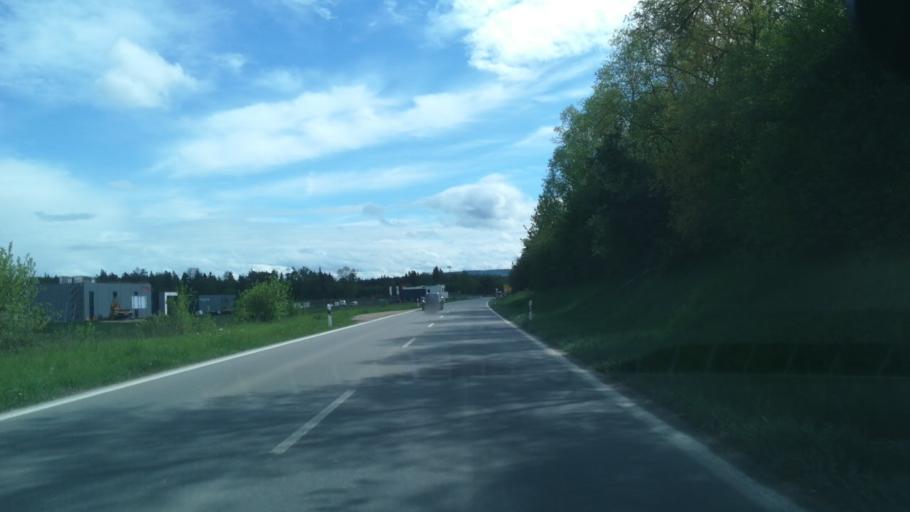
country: DE
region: Baden-Wuerttemberg
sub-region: Freiburg Region
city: Steisslingen
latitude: 47.7785
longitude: 8.9161
